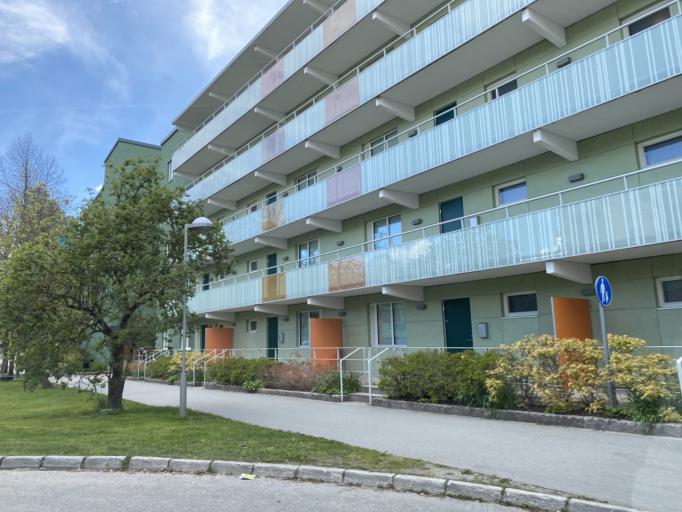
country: SE
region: Stockholm
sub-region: Stockholms Kommun
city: Kista
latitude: 59.4090
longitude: 17.9206
